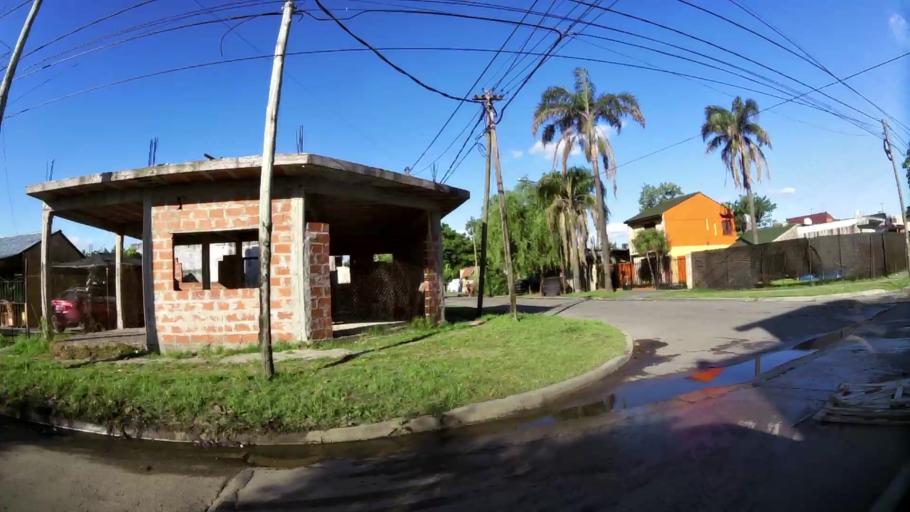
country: AR
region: Buenos Aires
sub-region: Partido de Moron
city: Moron
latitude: -34.6866
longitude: -58.6308
